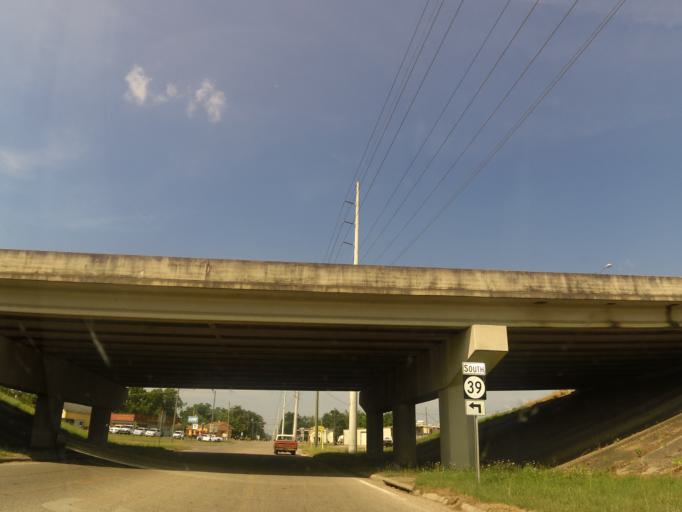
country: US
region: Mississippi
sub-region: Lauderdale County
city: Meridian
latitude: 32.3712
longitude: -88.6794
